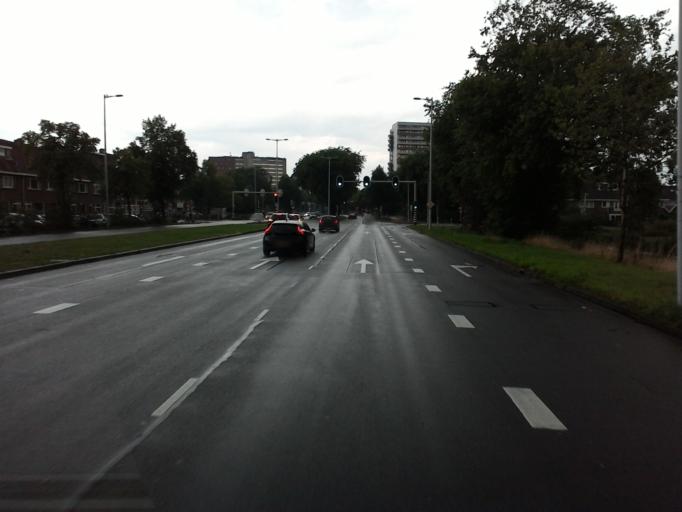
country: NL
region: Utrecht
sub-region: Gemeente Utrecht
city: Utrecht
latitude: 52.1054
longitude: 5.1221
